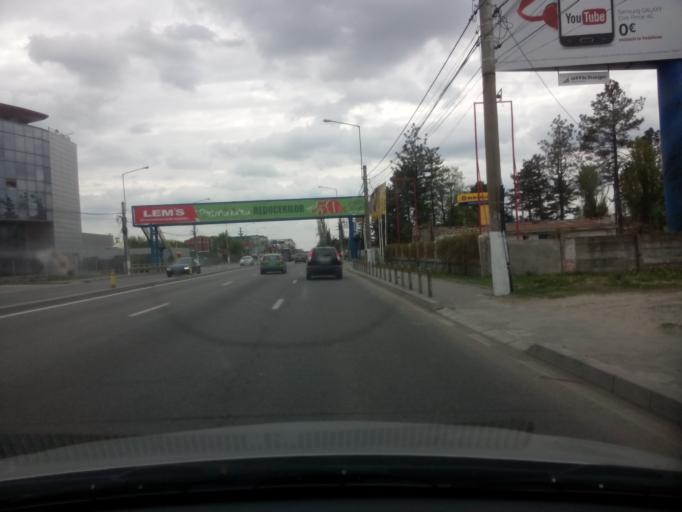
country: RO
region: Ilfov
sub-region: Comuna Otopeni
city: Otopeni
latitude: 44.5609
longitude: 26.0693
